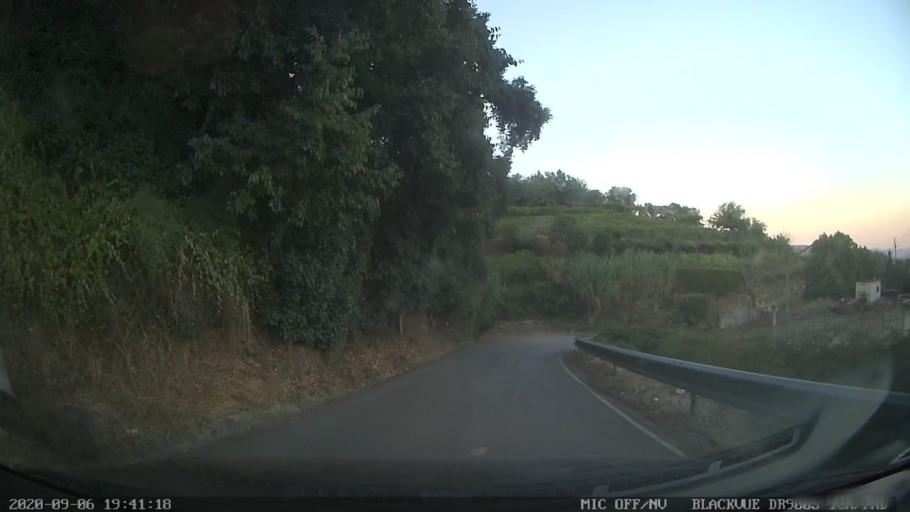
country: PT
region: Vila Real
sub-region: Mesao Frio
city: Mesao Frio
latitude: 41.1622
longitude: -7.8791
